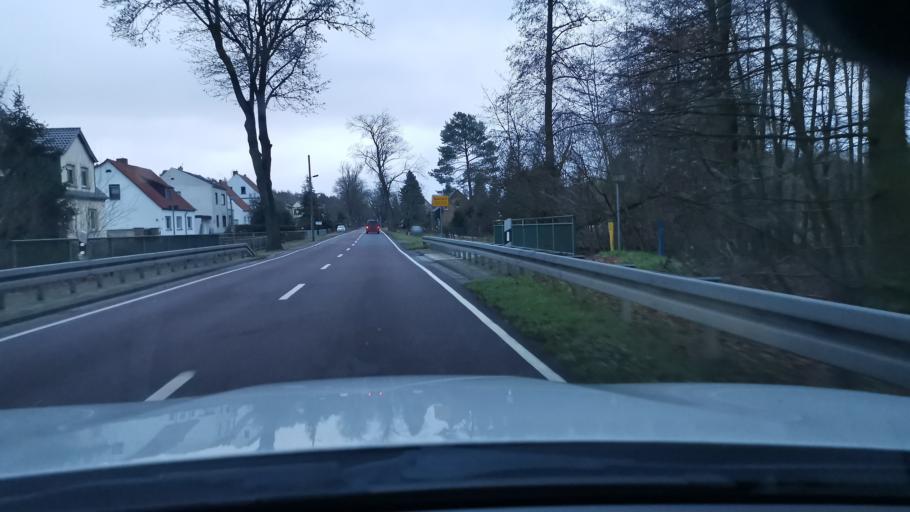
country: DE
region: Saxony-Anhalt
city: Nudersdorf
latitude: 51.9412
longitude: 12.6006
